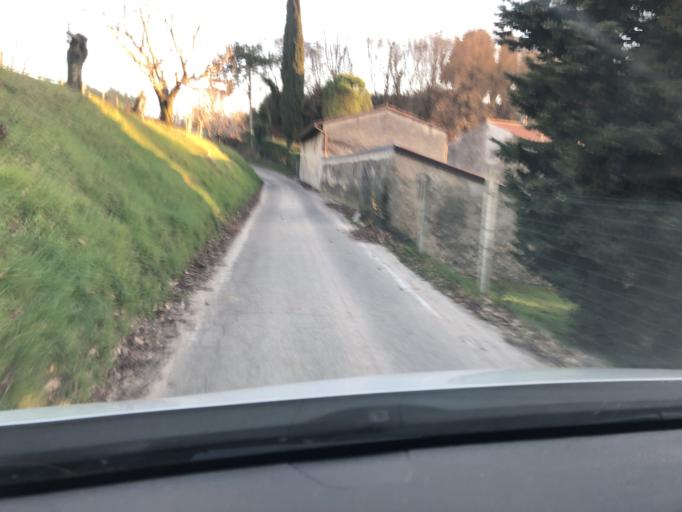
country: IT
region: Veneto
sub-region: Provincia di Verona
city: Sandra
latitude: 45.4670
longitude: 10.8038
